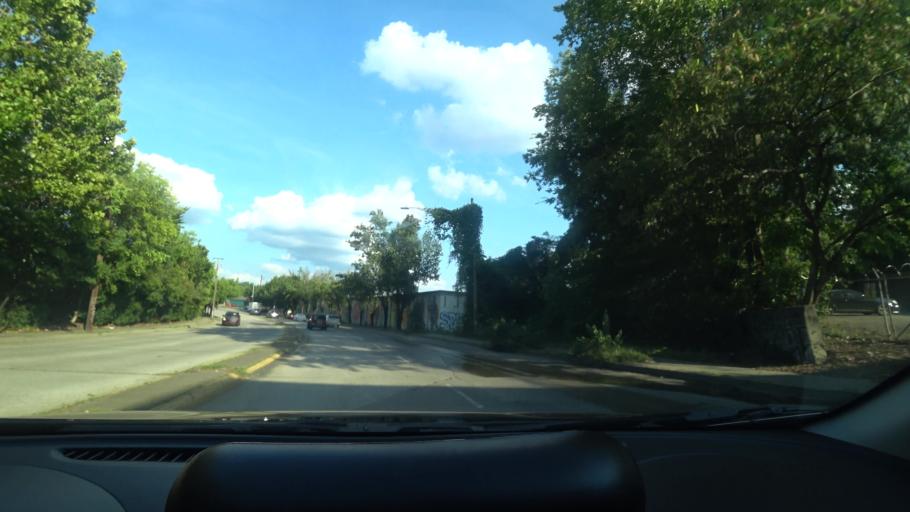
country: US
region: Georgia
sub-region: Fulton County
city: Atlanta
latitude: 33.7370
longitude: -84.4062
